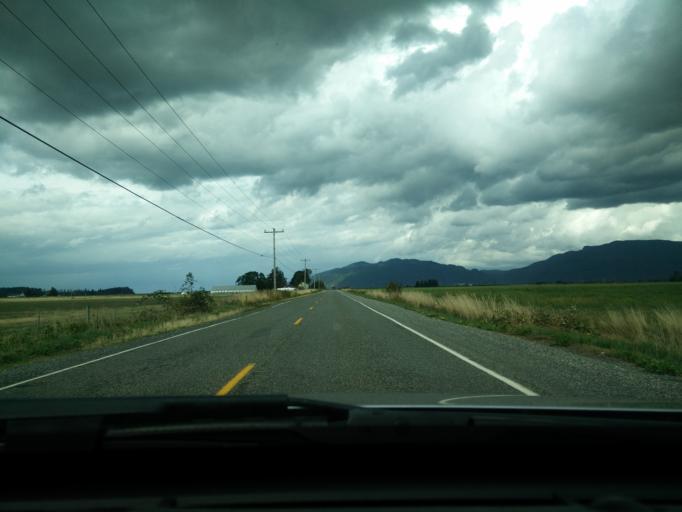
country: US
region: Washington
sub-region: Skagit County
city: Anacortes
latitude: 48.5411
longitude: -122.4720
